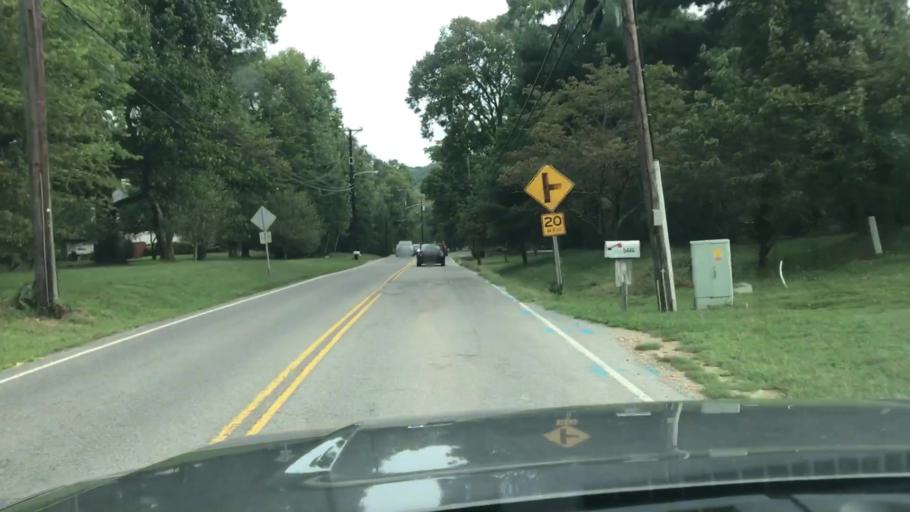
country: US
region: Tennessee
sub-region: Davidson County
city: Forest Hills
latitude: 36.0580
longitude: -86.8154
